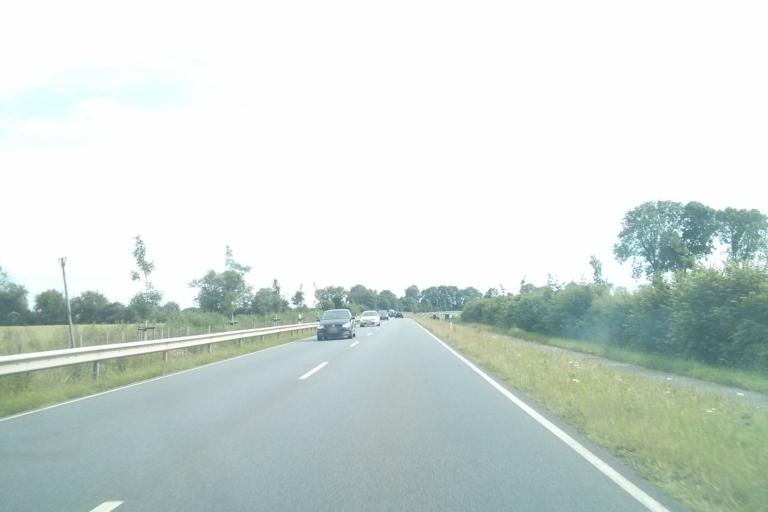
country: DE
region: Lower Saxony
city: Achim
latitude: 52.9885
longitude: 9.0535
